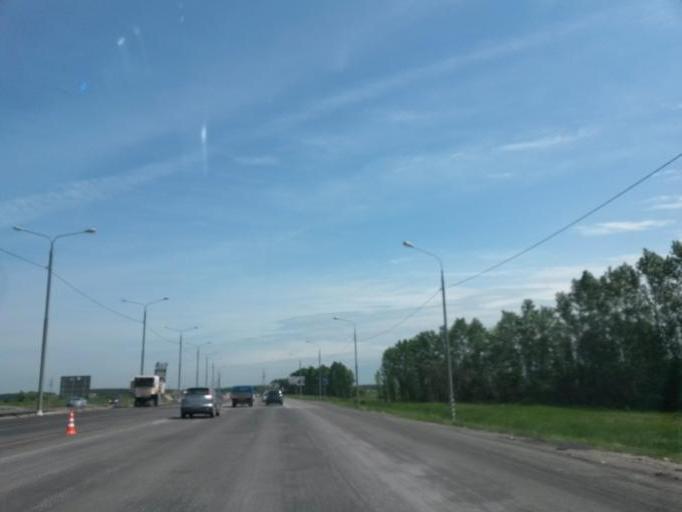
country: RU
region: Moskovskaya
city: Klimovsk
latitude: 55.3390
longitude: 37.5791
